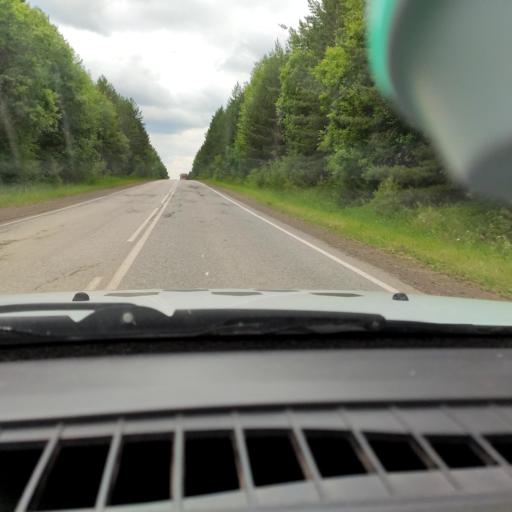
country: RU
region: Perm
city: Kukushtan
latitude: 57.3157
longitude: 56.5586
